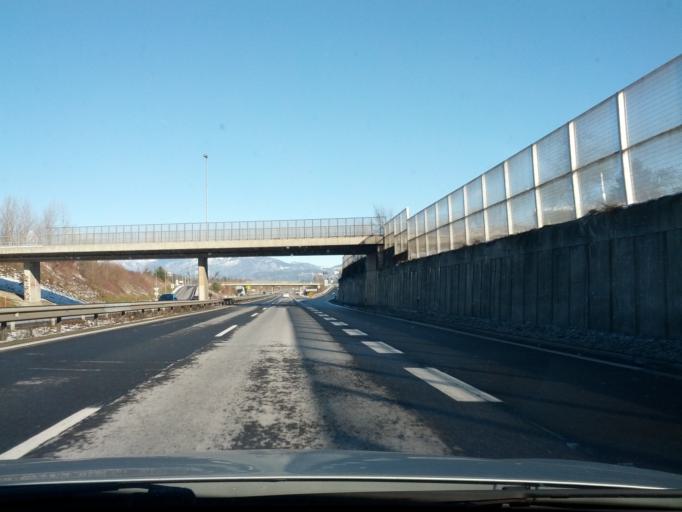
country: SI
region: Dol pri Ljubljani
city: Dol pri Ljubljani
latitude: 46.0879
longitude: 14.5855
